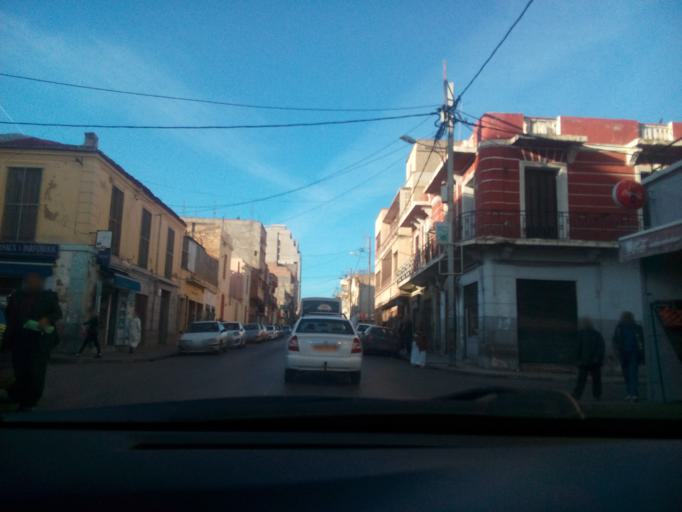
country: DZ
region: Oran
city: Oran
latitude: 35.6897
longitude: -0.6587
